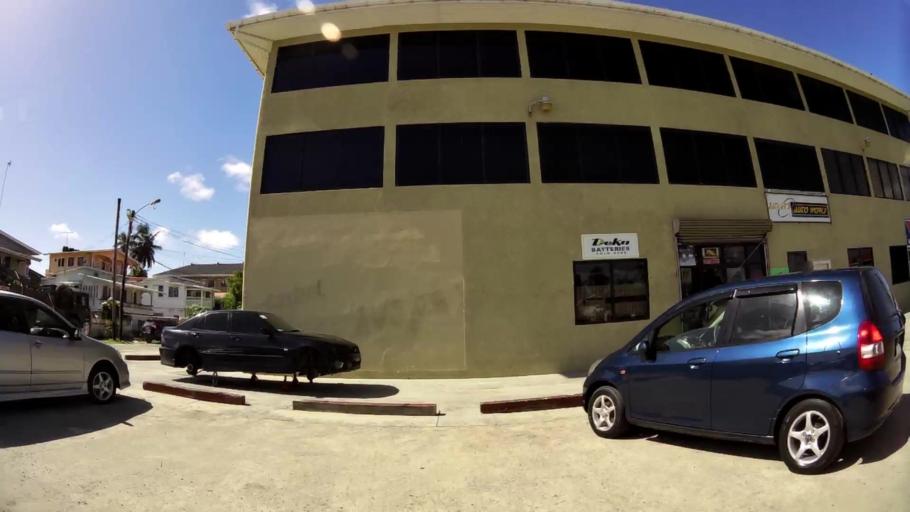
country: GY
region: Demerara-Mahaica
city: Georgetown
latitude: 6.8135
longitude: -58.1371
